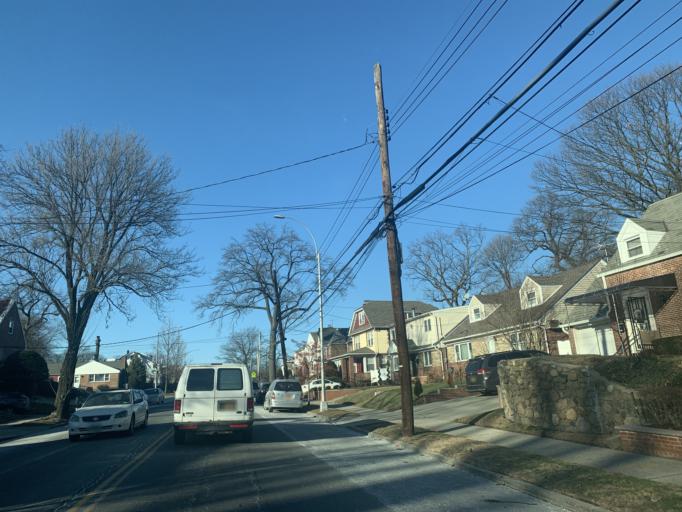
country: US
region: New York
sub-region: Queens County
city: Jamaica
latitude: 40.7199
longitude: -73.7758
